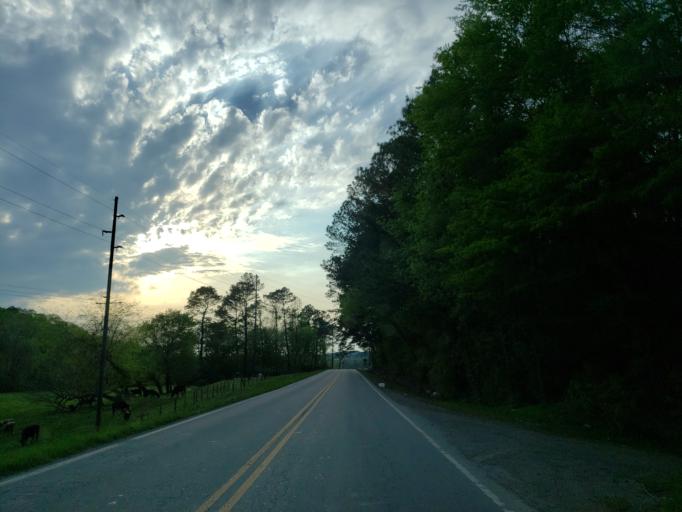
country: US
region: Georgia
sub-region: Cherokee County
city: Ball Ground
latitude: 34.2994
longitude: -84.3975
